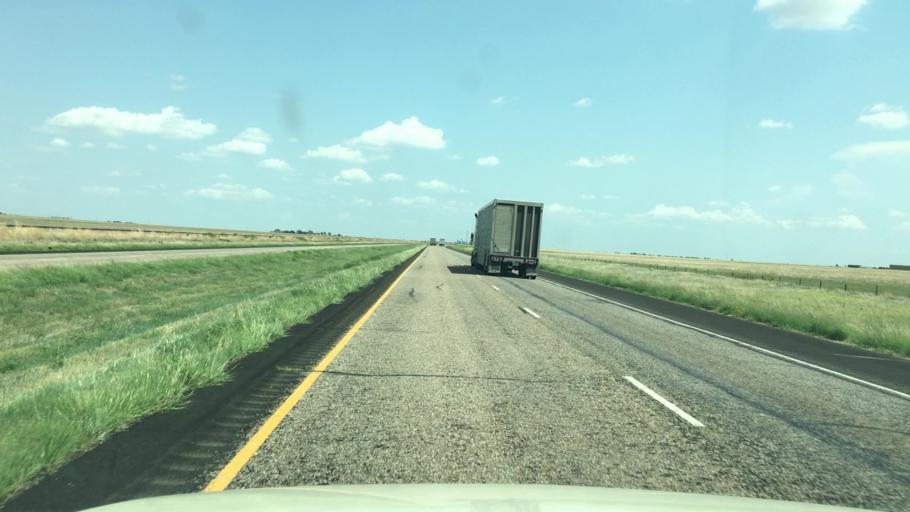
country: US
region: Texas
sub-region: Armstrong County
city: Claude
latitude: 35.1279
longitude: -101.4050
